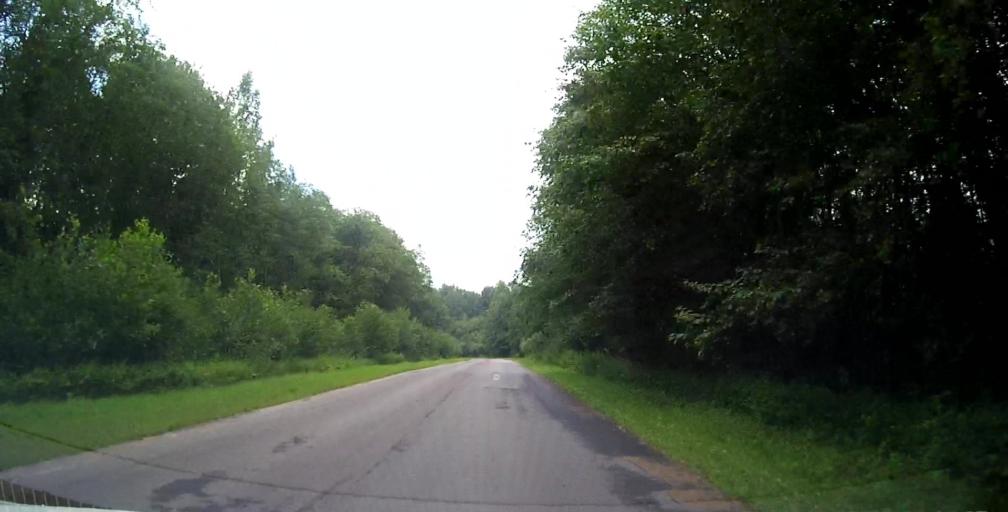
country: RU
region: Smolensk
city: Demidov
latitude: 55.4742
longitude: 31.6350
